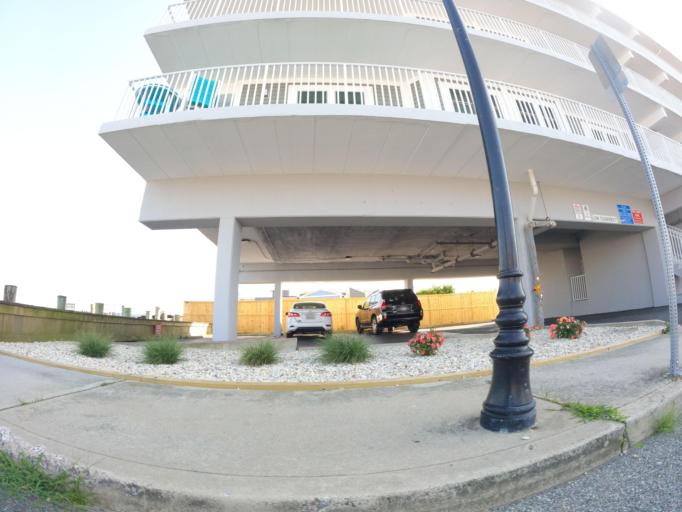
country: US
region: Maryland
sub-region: Worcester County
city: Ocean City
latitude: 38.3299
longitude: -75.0893
